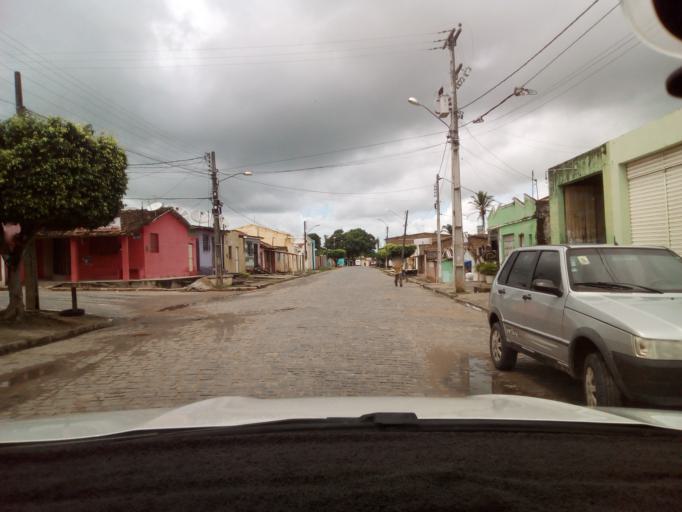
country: BR
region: Paraiba
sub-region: Pedras De Fogo
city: Pedras de Fogo
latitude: -7.4077
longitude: -35.1133
